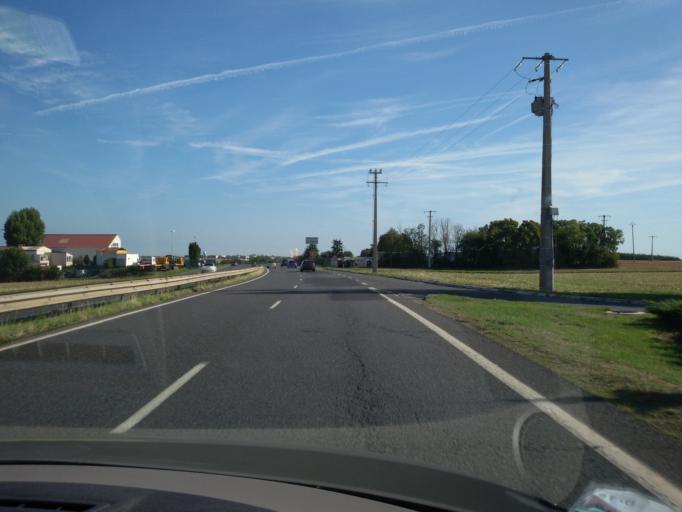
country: FR
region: Ile-de-France
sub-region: Departement de l'Essonne
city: Etampes
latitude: 48.4097
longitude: 2.1266
